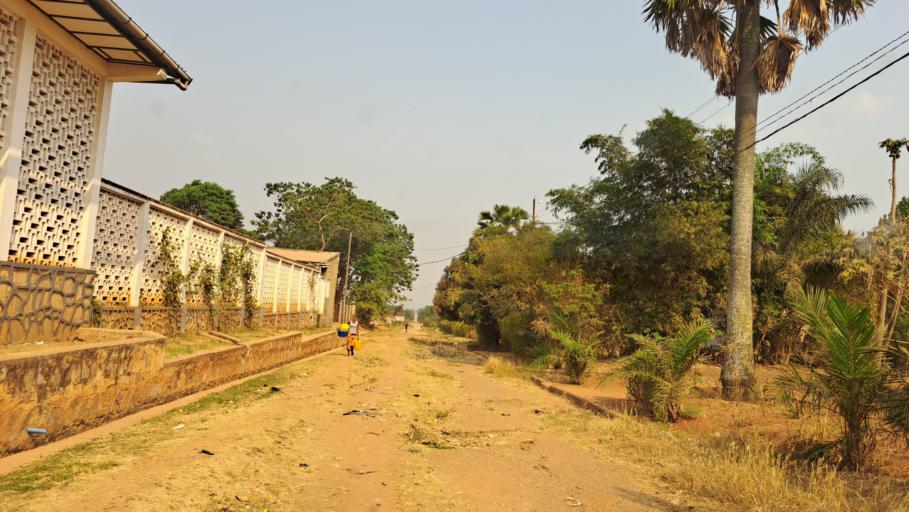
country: CD
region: Kasai-Oriental
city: Mbuji-Mayi
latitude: -6.1317
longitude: 23.5860
